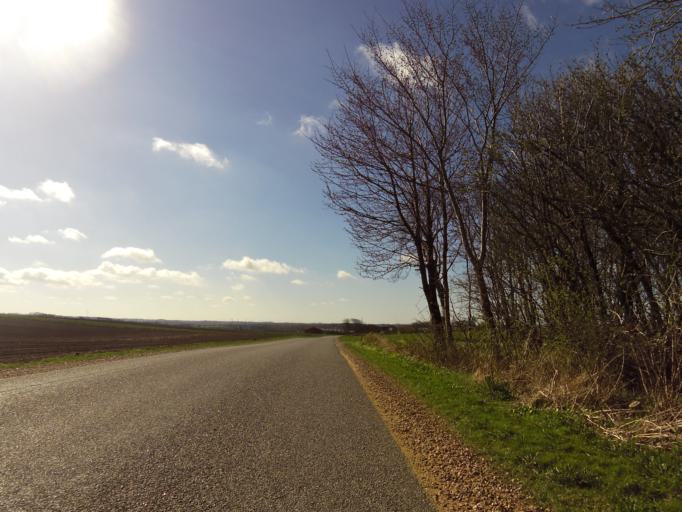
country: DK
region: Central Jutland
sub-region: Holstebro Kommune
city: Vinderup
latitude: 56.4545
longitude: 8.7231
